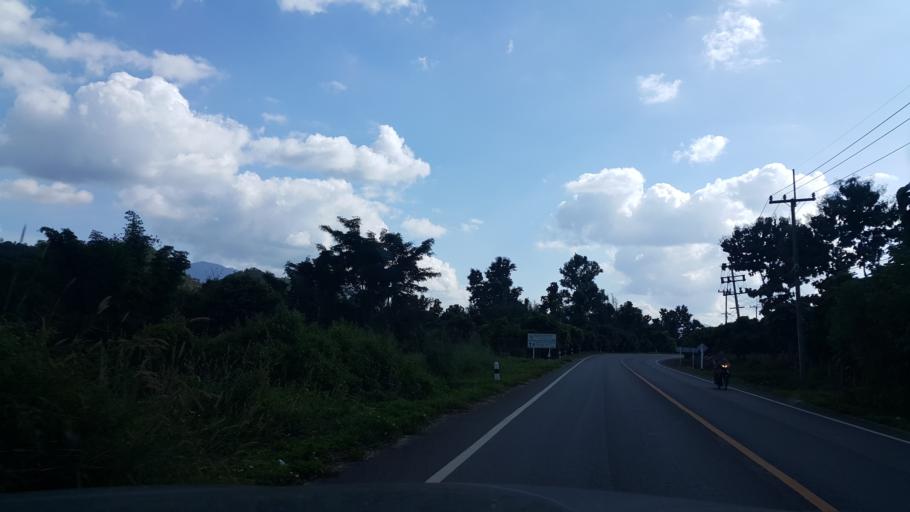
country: TH
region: Lamphun
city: Ban Thi
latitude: 18.5770
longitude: 99.2594
